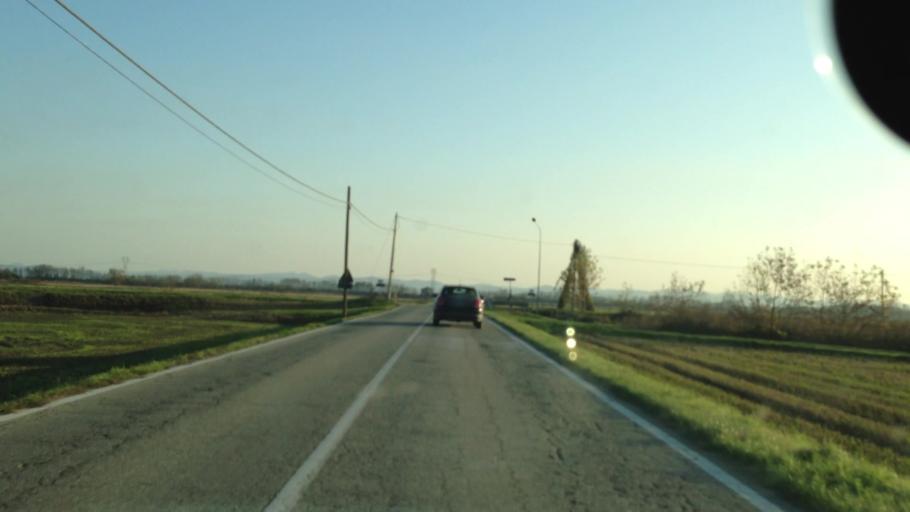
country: IT
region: Piedmont
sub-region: Provincia di Vercelli
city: Lamporo
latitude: 45.2541
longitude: 8.0869
